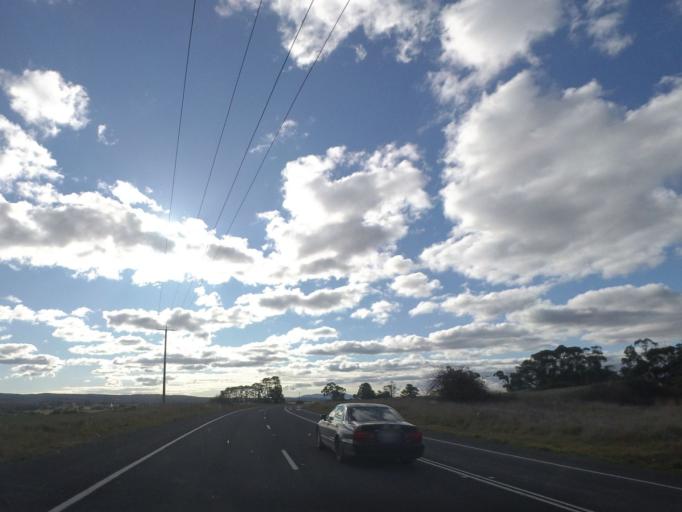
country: AU
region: Victoria
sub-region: Mount Alexander
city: Castlemaine
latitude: -37.1778
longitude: 144.3596
